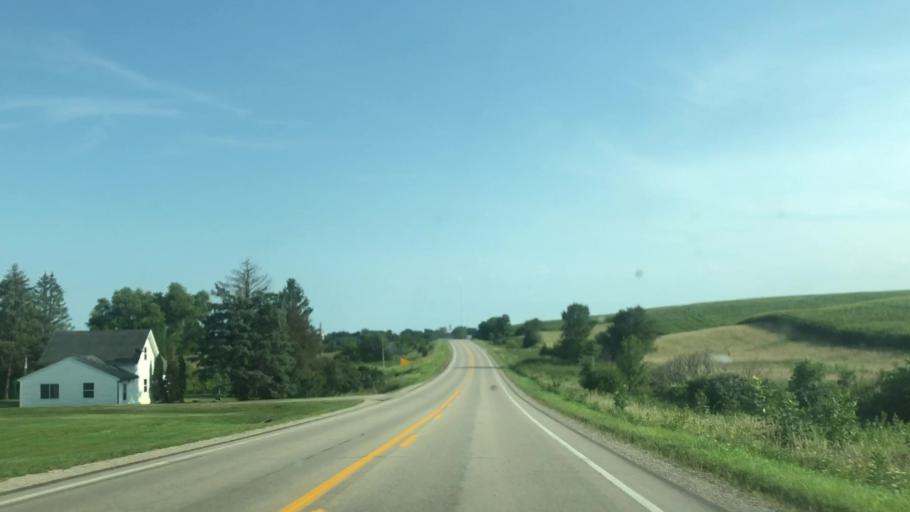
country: US
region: Iowa
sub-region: Marshall County
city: Marshalltown
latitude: 42.0384
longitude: -93.0001
